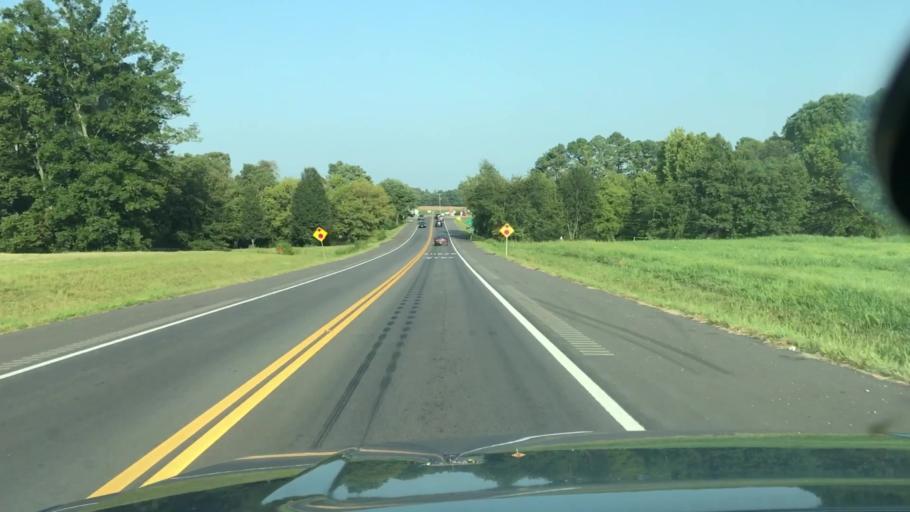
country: US
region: Tennessee
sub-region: Sumner County
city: Portland
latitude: 36.5905
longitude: -86.5961
